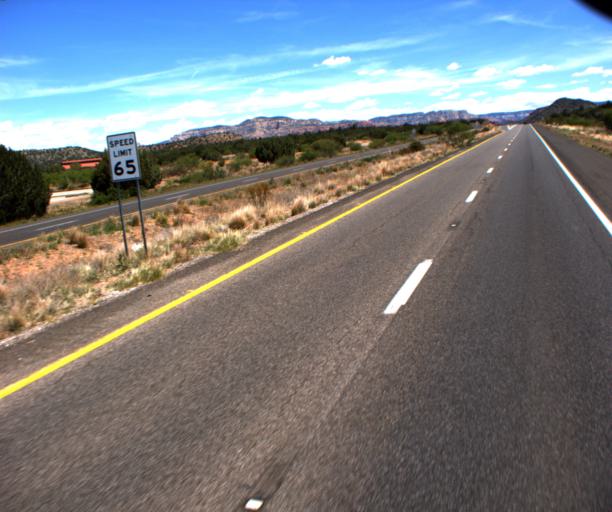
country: US
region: Arizona
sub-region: Yavapai County
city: West Sedona
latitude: 34.8292
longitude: -111.8940
